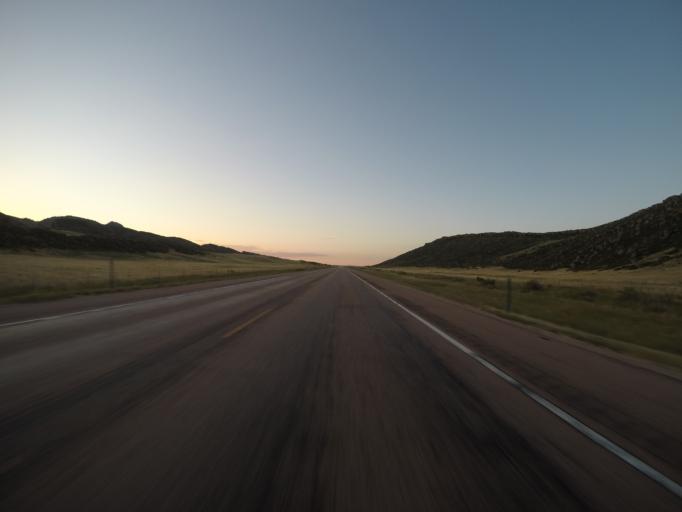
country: US
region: Colorado
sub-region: Larimer County
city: Laporte
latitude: 40.7097
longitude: -105.1729
